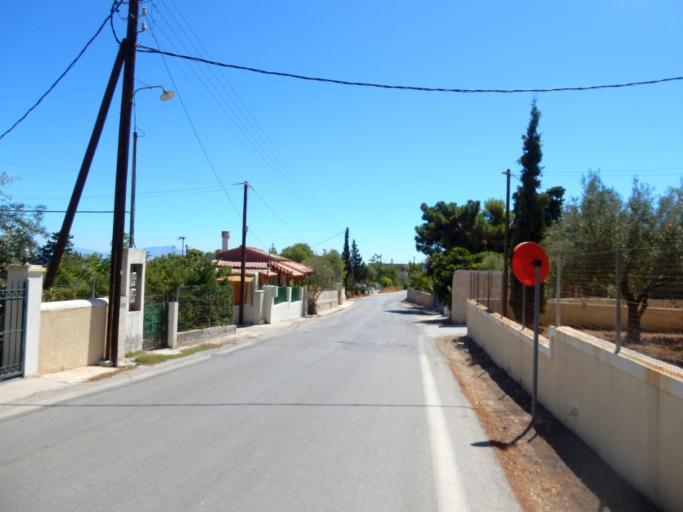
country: GR
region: Attica
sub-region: Nomos Piraios
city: Vathi
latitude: 37.7723
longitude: 23.5054
